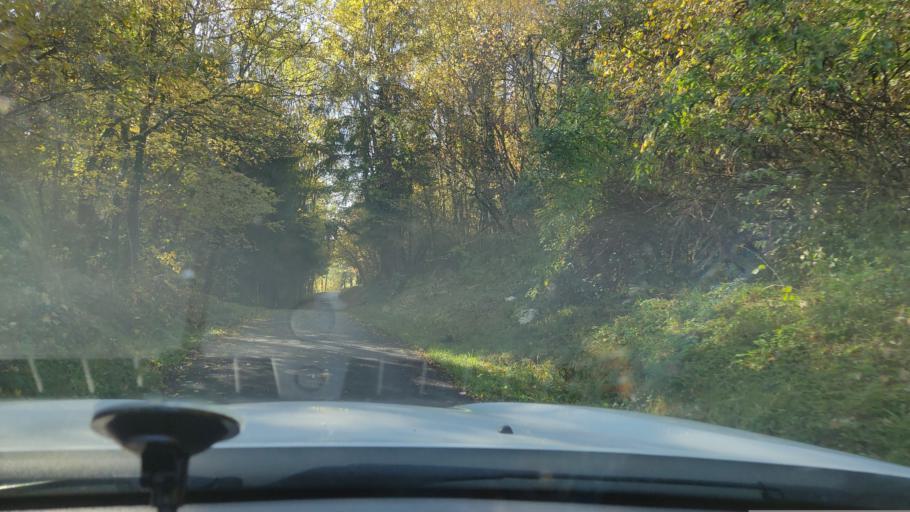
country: FR
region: Rhone-Alpes
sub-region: Departement de la Savoie
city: Vimines
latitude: 45.5132
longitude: 5.8365
